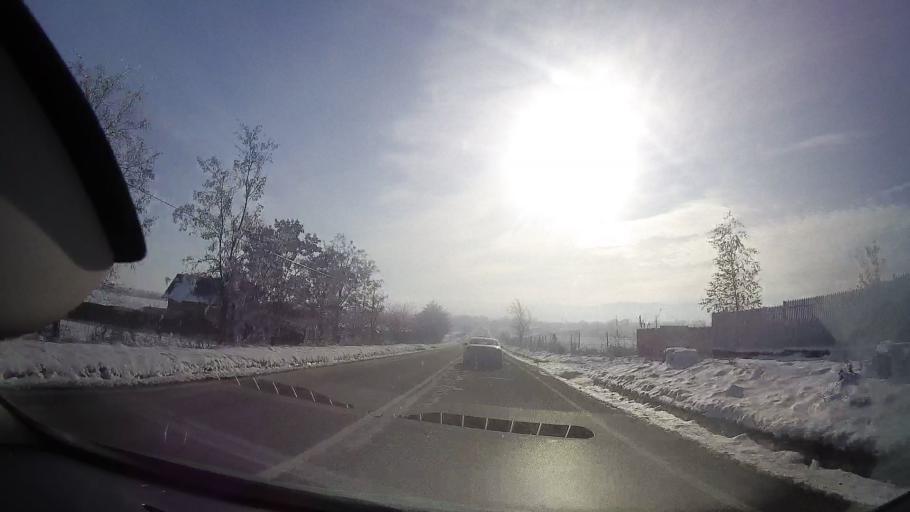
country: RO
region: Neamt
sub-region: Comuna Dobreni
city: Dobreni
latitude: 47.0070
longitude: 26.4244
